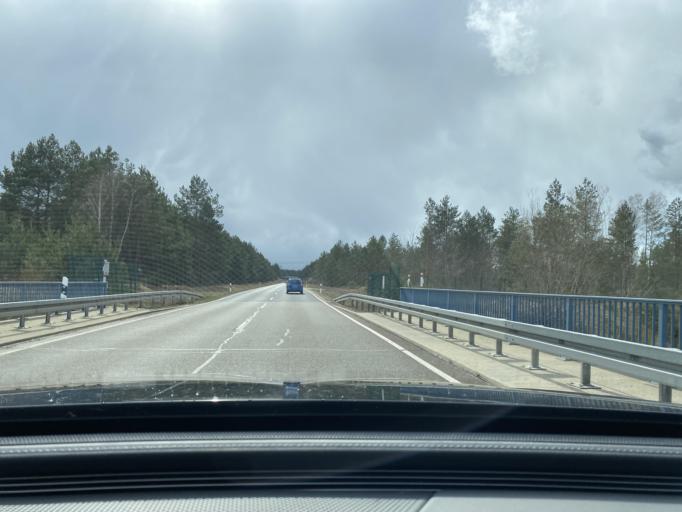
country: DE
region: Saxony
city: Boxberg
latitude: 51.4180
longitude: 14.5956
